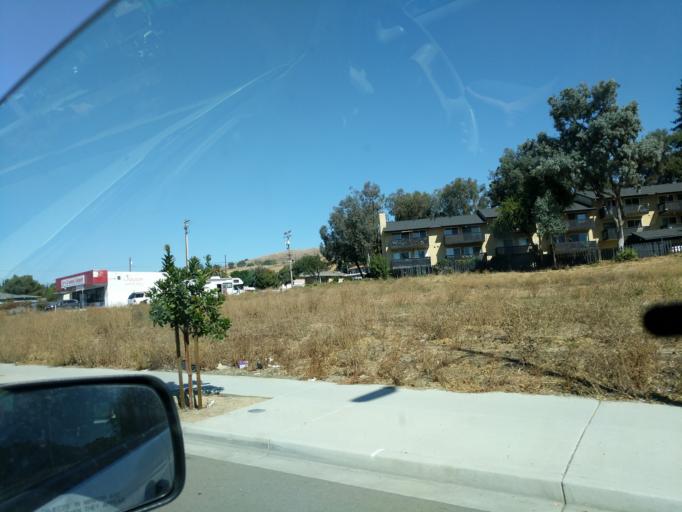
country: US
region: California
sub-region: Alameda County
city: Hayward
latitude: 37.6396
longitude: -122.0576
